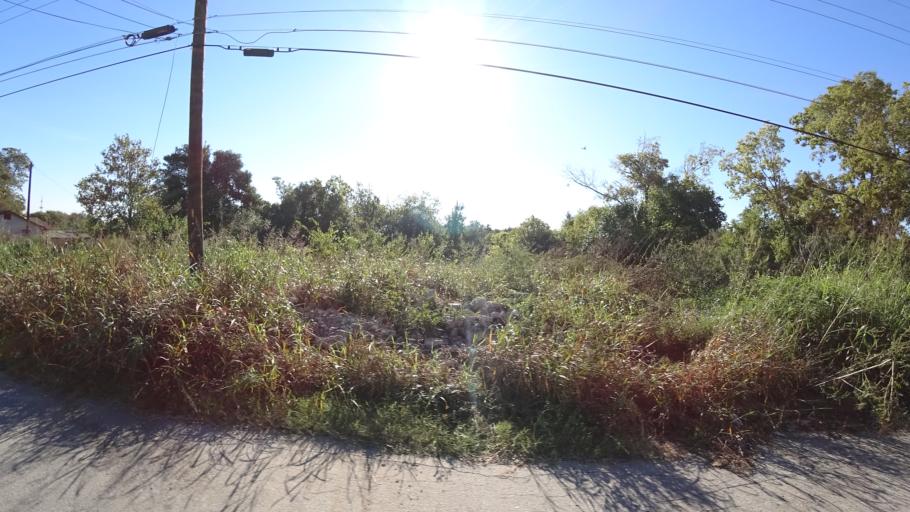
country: US
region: Texas
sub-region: Travis County
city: Austin
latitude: 30.2202
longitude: -97.7023
